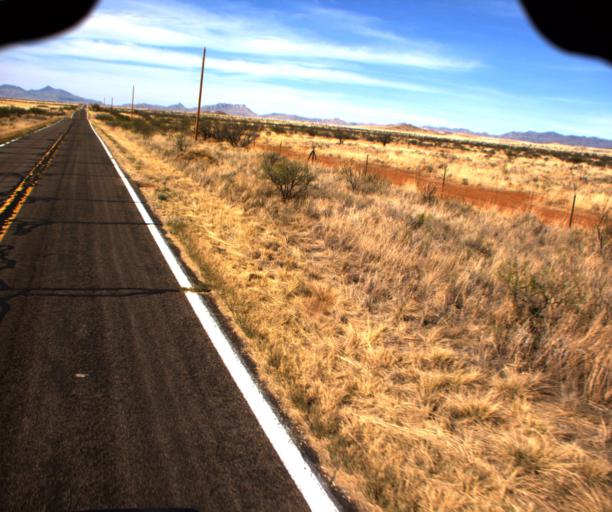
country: US
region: Arizona
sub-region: Cochise County
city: Willcox
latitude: 31.9084
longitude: -109.4914
